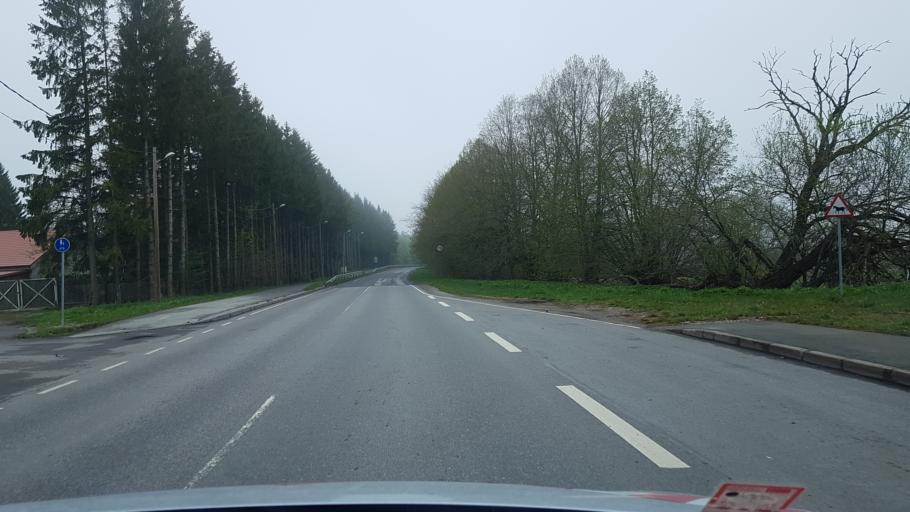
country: EE
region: Harju
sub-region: Joelaehtme vald
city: Loo
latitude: 59.4161
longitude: 24.9447
